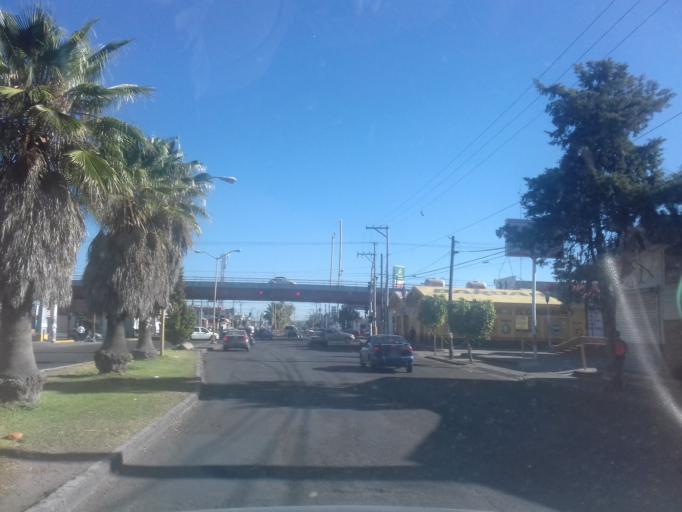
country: MX
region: Aguascalientes
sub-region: Aguascalientes
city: Aguascalientes
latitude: 21.8591
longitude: -102.2694
